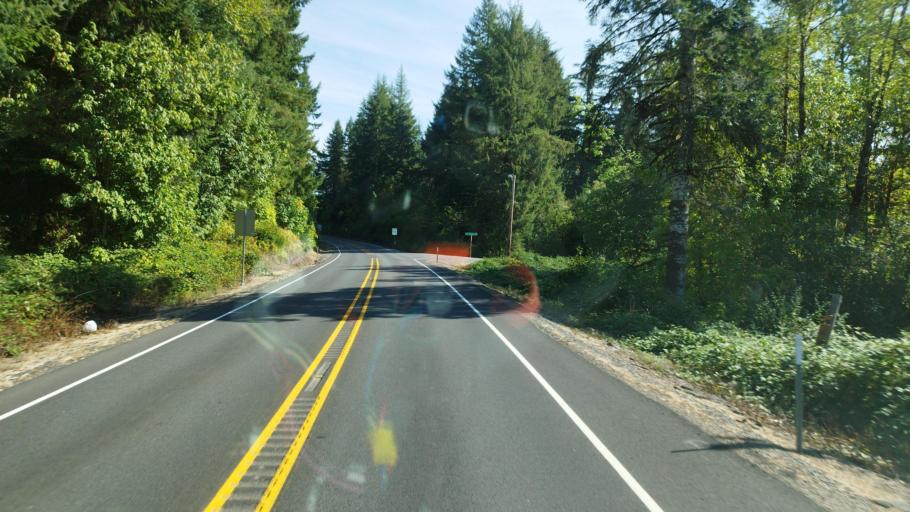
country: US
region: Oregon
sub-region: Clatsop County
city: Seaside
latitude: 45.8647
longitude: -123.5916
